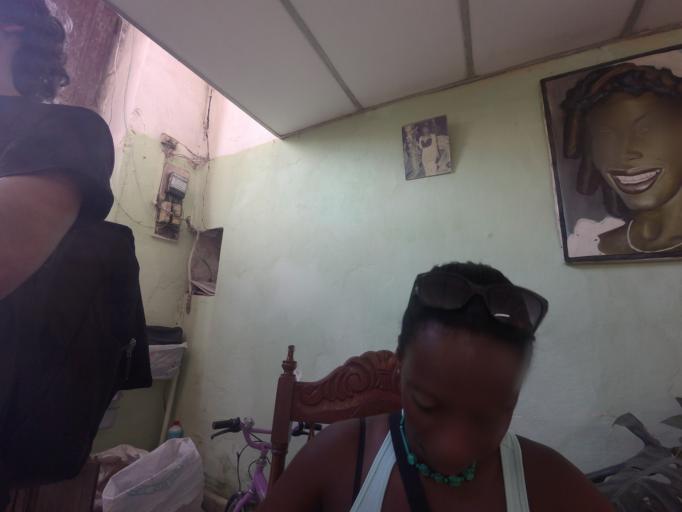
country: CU
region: La Habana
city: La Habana Vieja
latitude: 23.1299
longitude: -82.3514
